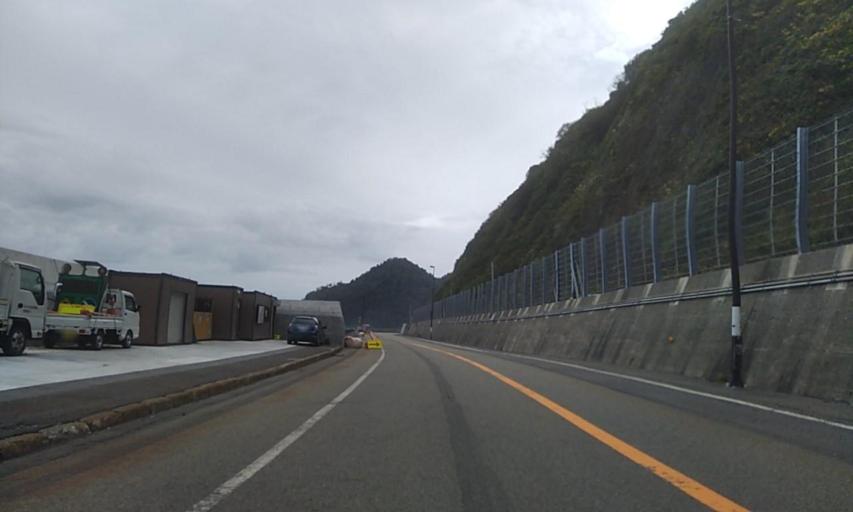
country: JP
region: Hokkaido
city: Obihiro
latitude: 42.1311
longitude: 143.3177
